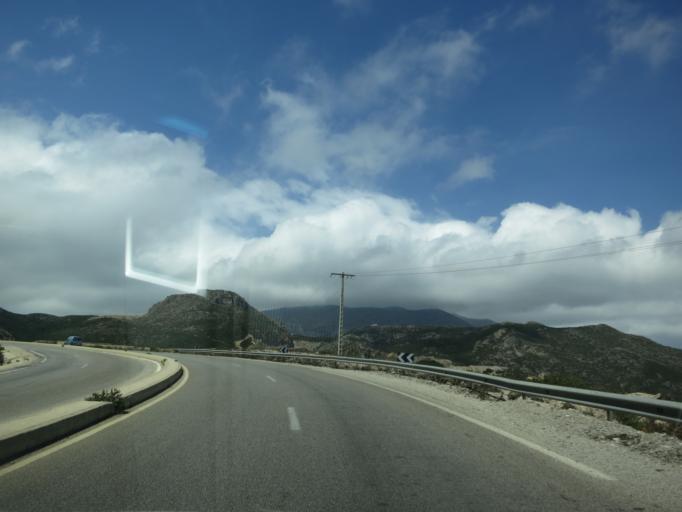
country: ES
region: Ceuta
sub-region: Ceuta
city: Ceuta
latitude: 35.8687
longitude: -5.3827
